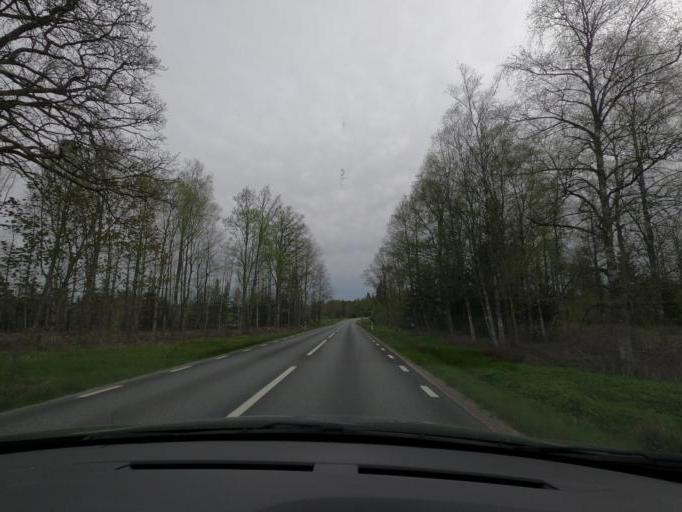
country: SE
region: Joenkoeping
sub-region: Varnamo Kommun
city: Bredaryd
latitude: 57.1883
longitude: 13.7580
